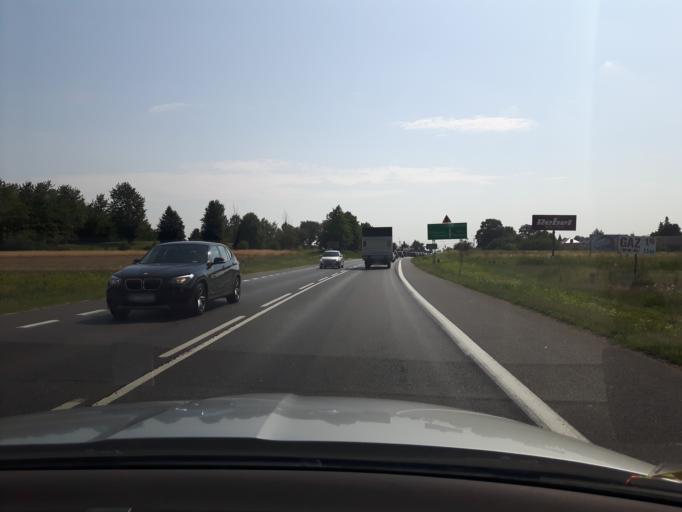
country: PL
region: Masovian Voivodeship
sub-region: Powiat mlawski
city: Mlawa
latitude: 53.1070
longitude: 20.4003
